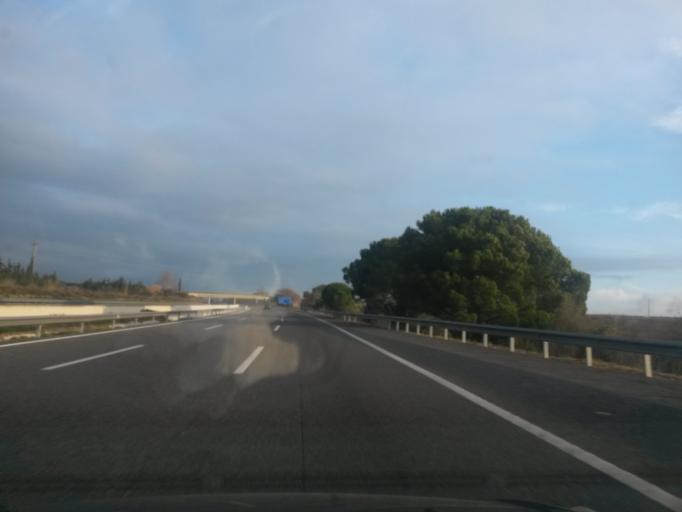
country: ES
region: Catalonia
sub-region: Provincia de Girona
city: Vilafant
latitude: 42.2517
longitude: 2.9436
